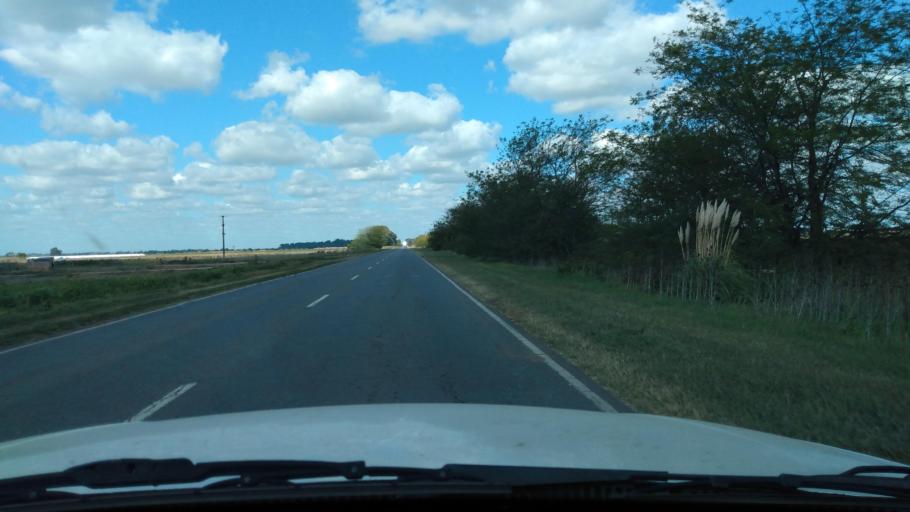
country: AR
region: Buenos Aires
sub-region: Partido de Navarro
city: Navarro
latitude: -34.9695
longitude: -59.3175
